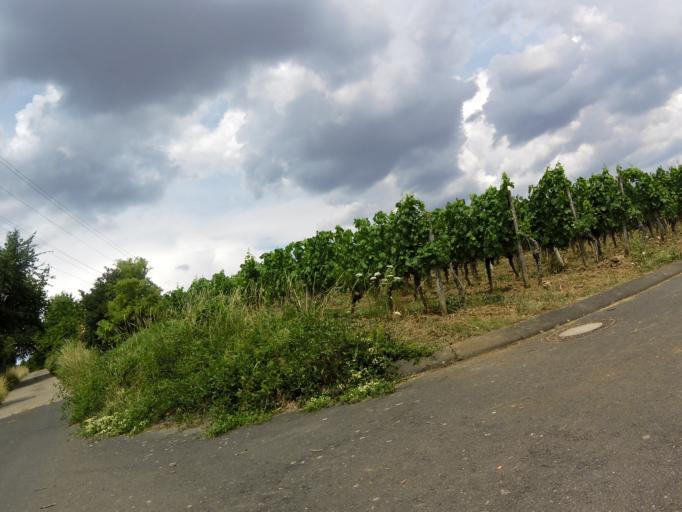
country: DE
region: Bavaria
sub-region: Regierungsbezirk Unterfranken
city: Randersacker
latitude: 49.7642
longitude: 9.9850
